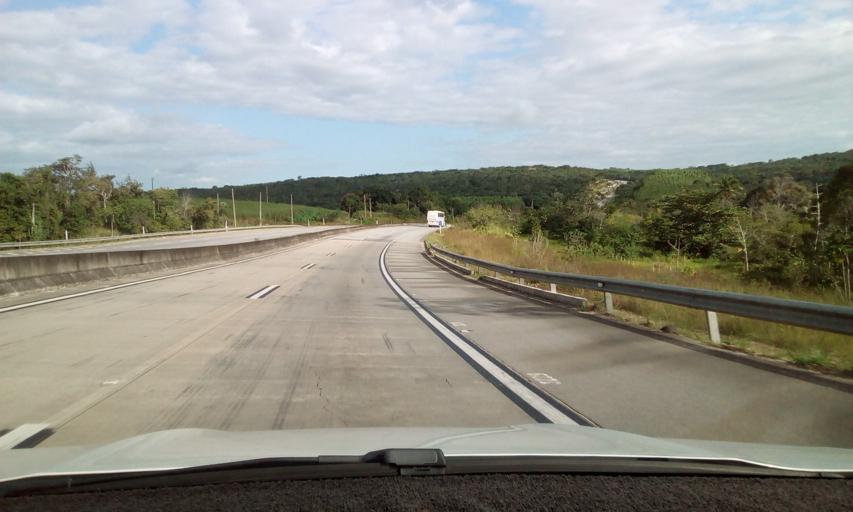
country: BR
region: Paraiba
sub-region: Cruz Do Espirito Santo
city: Cruz do Espirito Santo
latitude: -7.0083
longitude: -35.0612
